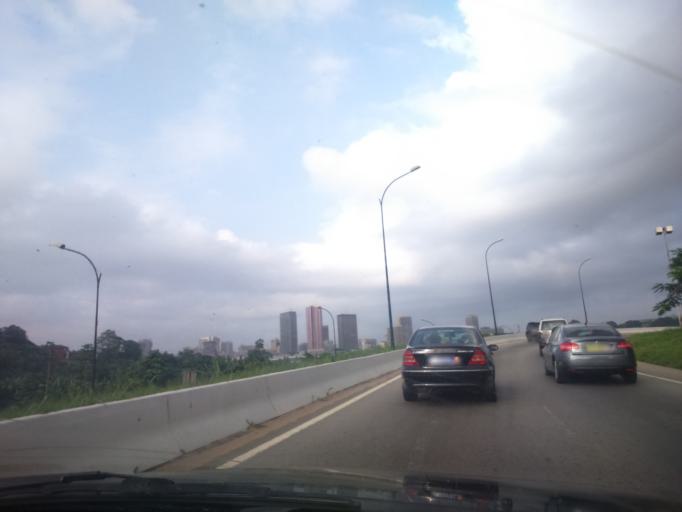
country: CI
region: Lagunes
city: Abidjan
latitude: 5.3353
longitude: -4.0117
